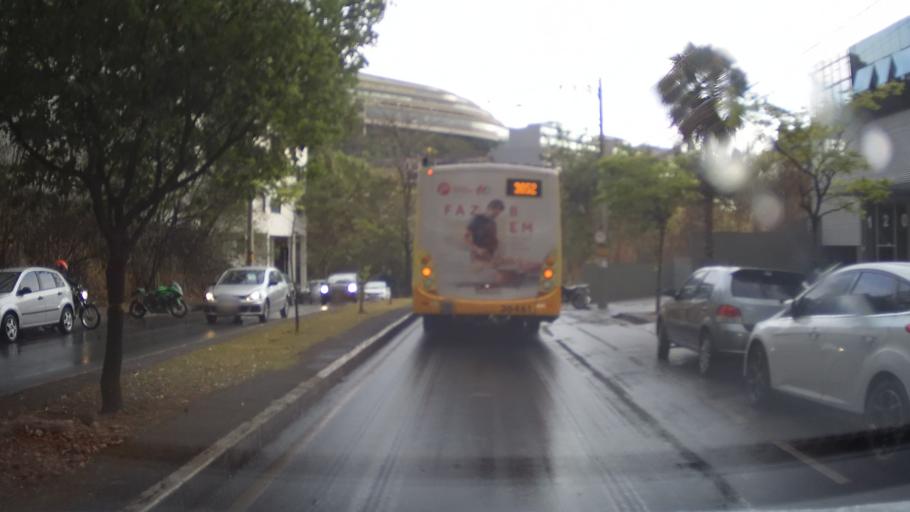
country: BR
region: Minas Gerais
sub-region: Belo Horizonte
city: Belo Horizonte
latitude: -19.9676
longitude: -43.9553
